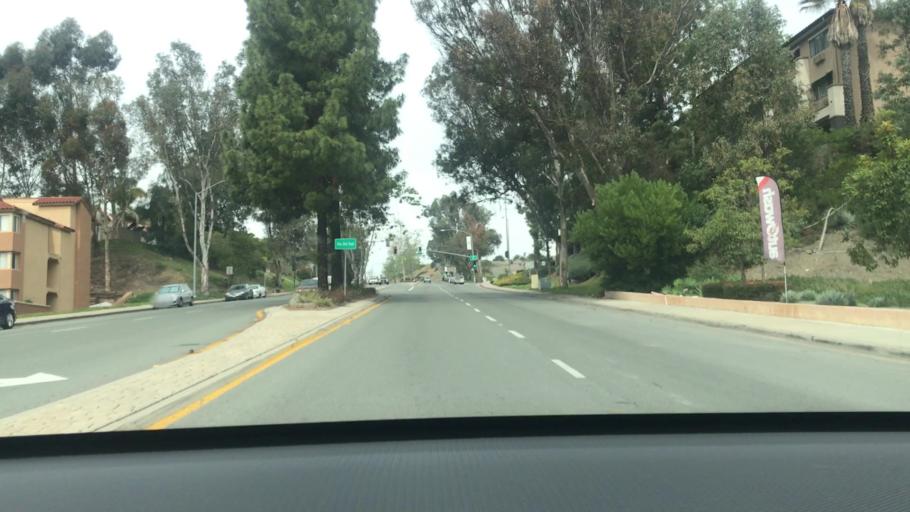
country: US
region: California
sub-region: San Diego County
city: Poway
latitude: 32.9523
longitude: -117.1080
